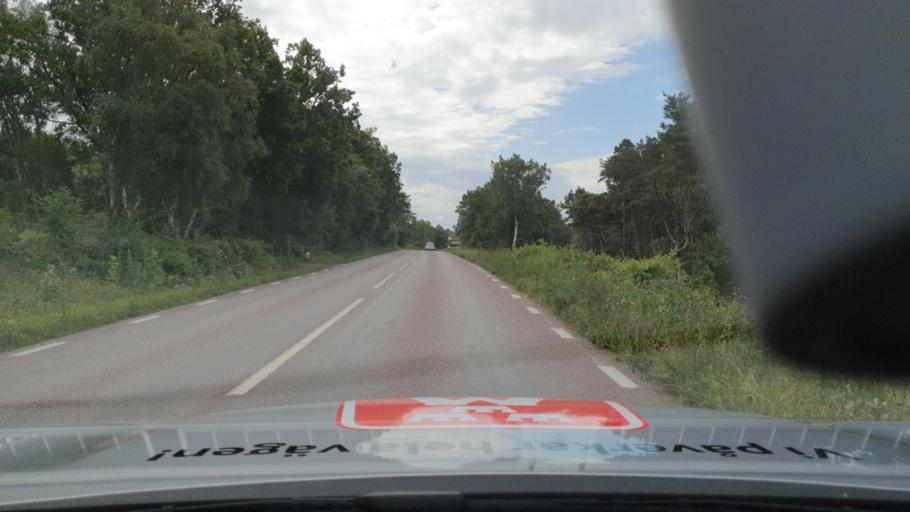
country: SE
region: Gotland
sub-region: Gotland
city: Hemse
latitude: 57.0777
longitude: 18.3003
